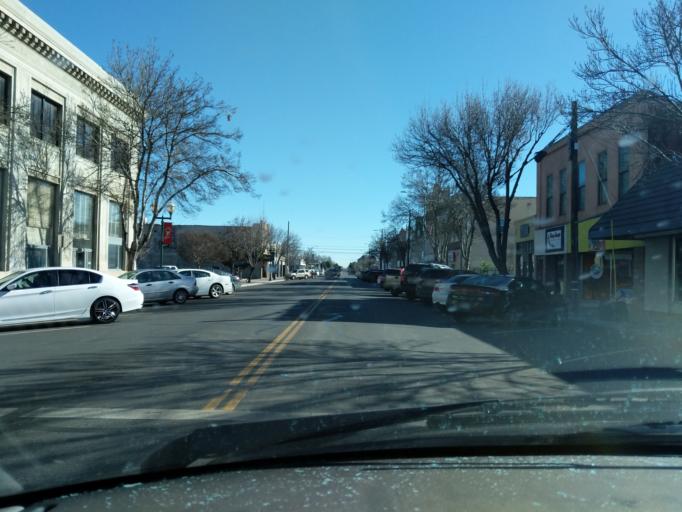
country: US
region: California
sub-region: Merced County
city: Los Banos
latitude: 37.0609
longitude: -120.8479
